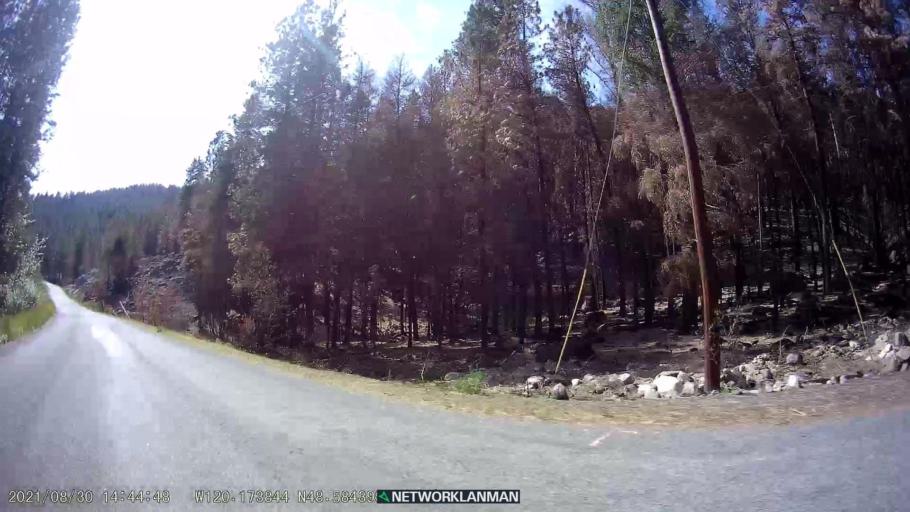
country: US
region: Washington
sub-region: Okanogan County
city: Brewster
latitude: 48.5849
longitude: -120.1739
